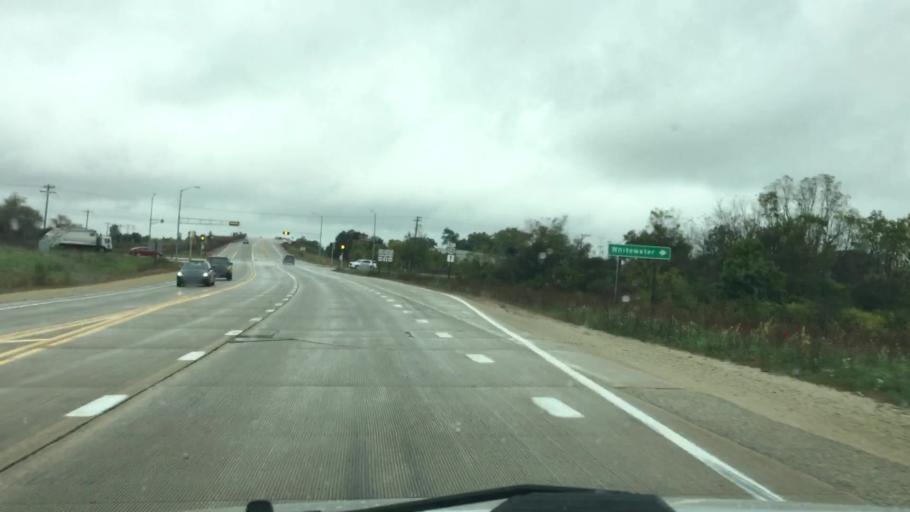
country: US
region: Wisconsin
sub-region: Walworth County
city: Whitewater
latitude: 42.8201
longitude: -88.7433
